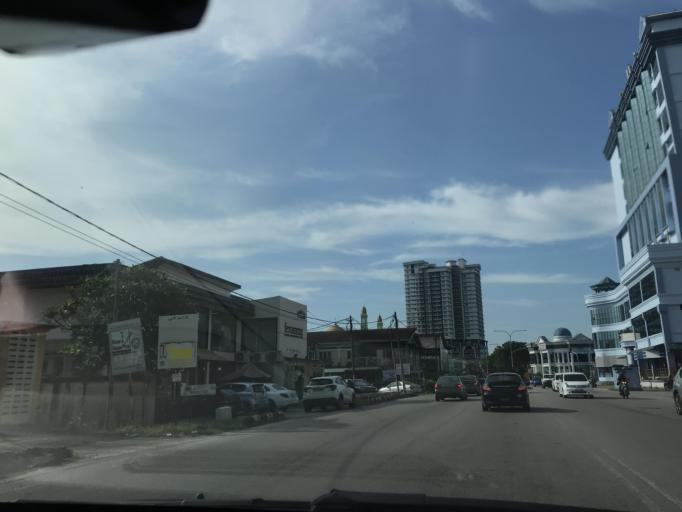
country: MY
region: Kelantan
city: Kota Bharu
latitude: 6.1261
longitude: 102.2472
